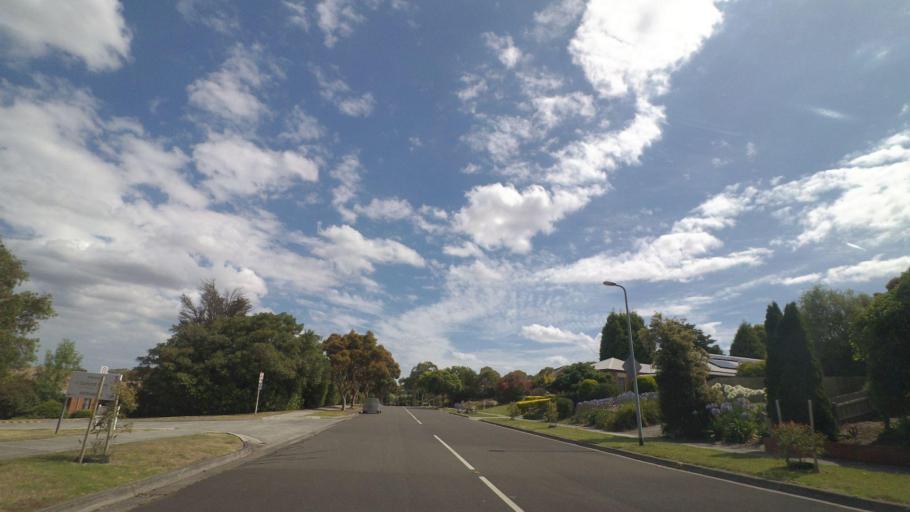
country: AU
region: Victoria
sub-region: Knox
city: Wantirna
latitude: -37.8533
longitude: 145.2266
